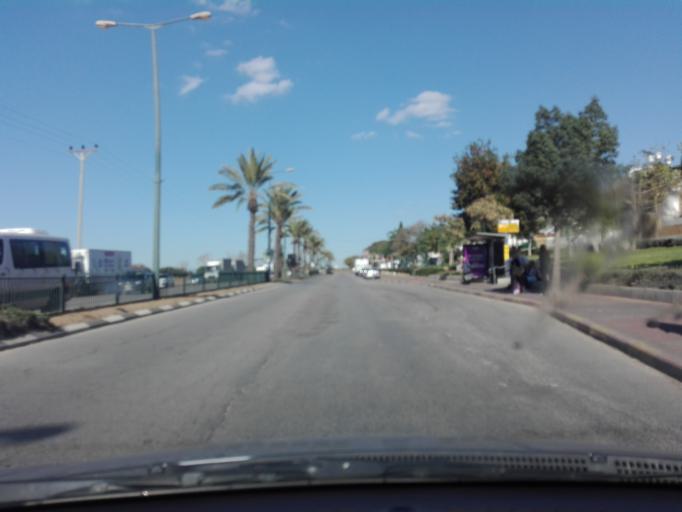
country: IL
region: Central District
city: Netanya
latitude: 32.3008
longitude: 34.8543
